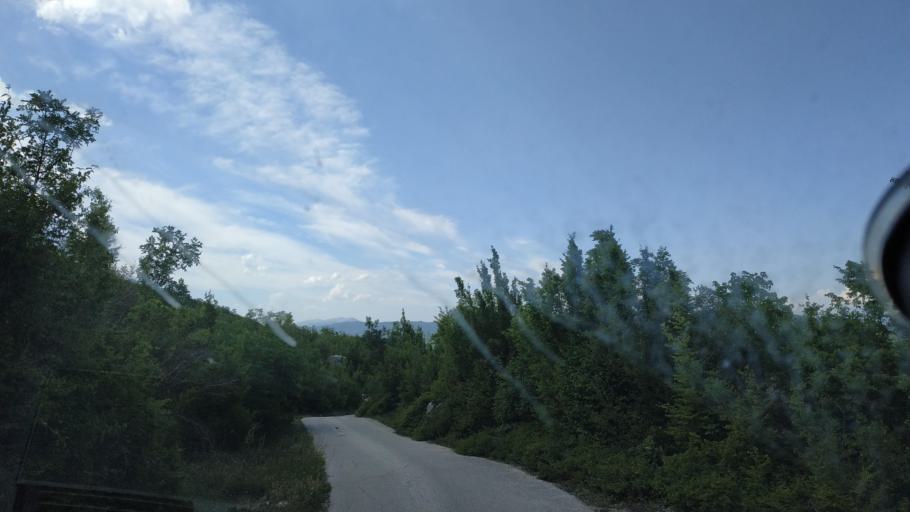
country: HR
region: Splitsko-Dalmatinska
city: Dugopolje
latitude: 43.5724
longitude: 16.6557
